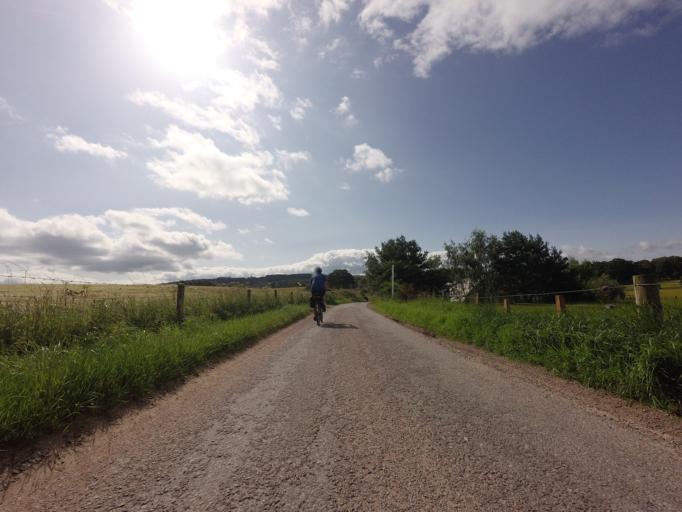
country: GB
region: Scotland
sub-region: Highland
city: Nairn
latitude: 57.5553
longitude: -3.8667
